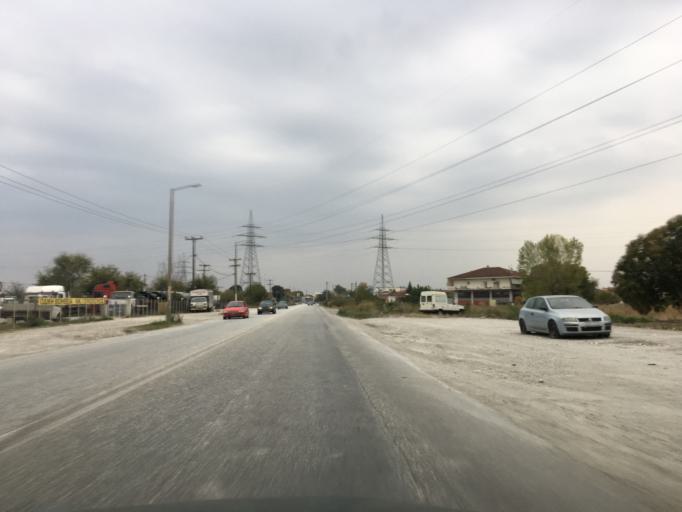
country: GR
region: Thessaly
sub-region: Trikala
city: Trikala
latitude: 39.5605
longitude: 21.7829
